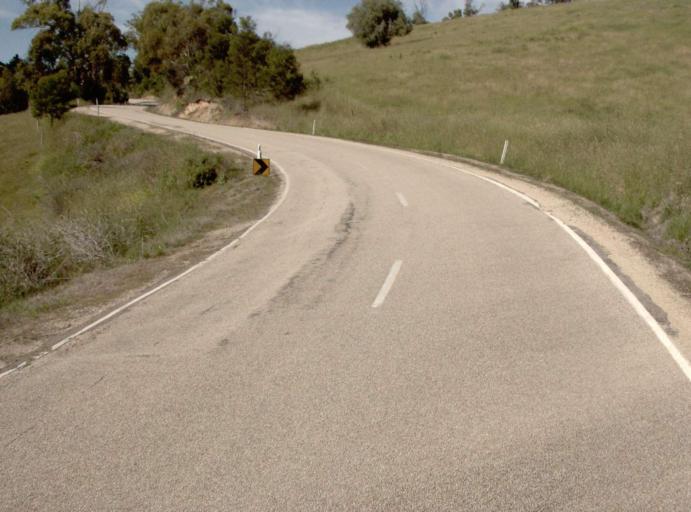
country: AU
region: Victoria
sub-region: East Gippsland
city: Lakes Entrance
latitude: -37.5114
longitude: 148.1681
